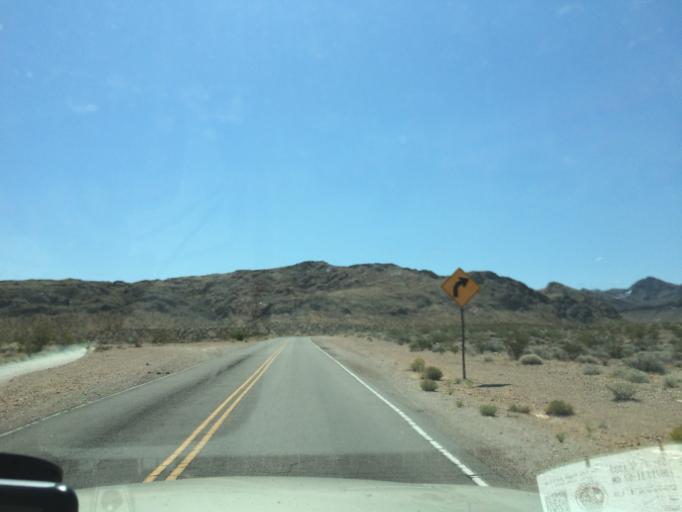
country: US
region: Nevada
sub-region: Clark County
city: Moapa Valley
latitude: 36.4310
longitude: -114.6299
